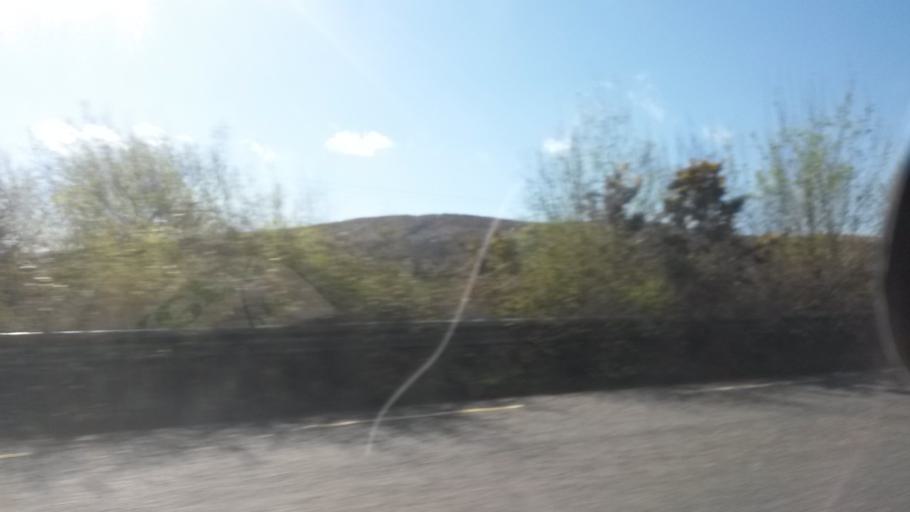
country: IE
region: Munster
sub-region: Ciarrai
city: Cill Airne
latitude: 51.9161
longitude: -9.3926
